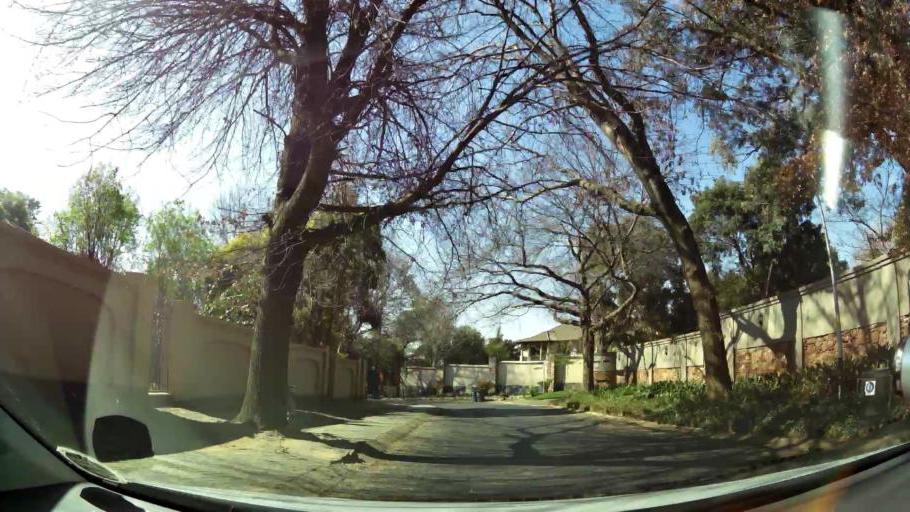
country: ZA
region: Gauteng
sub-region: City of Johannesburg Metropolitan Municipality
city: Modderfontein
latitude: -26.1611
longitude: 28.1223
